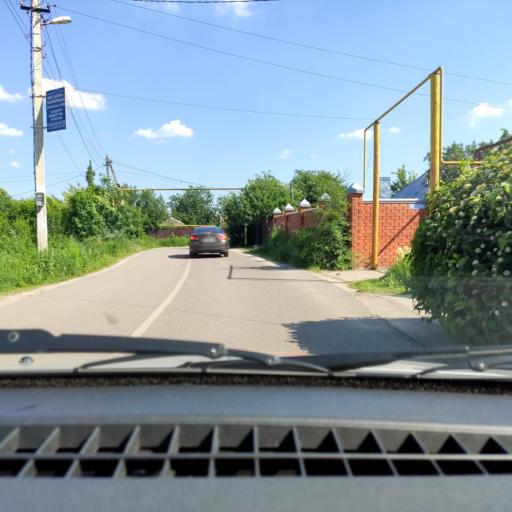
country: RU
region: Voronezj
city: Ramon'
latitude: 51.8191
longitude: 39.2666
